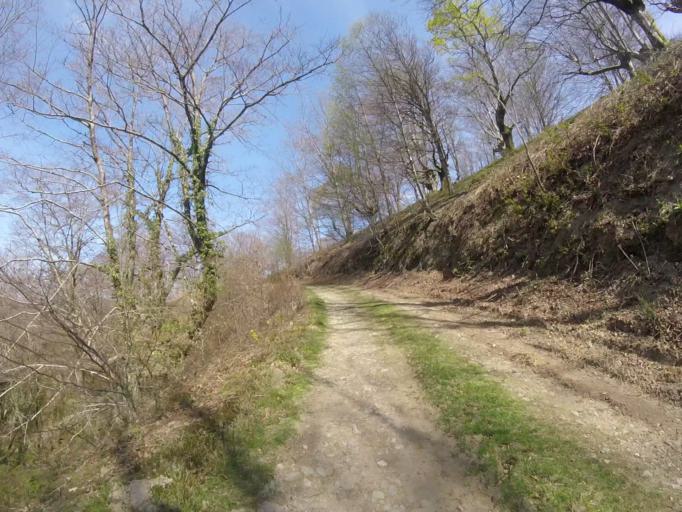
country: ES
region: Basque Country
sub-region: Provincia de Guipuzcoa
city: Irun
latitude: 43.2527
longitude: -1.8120
